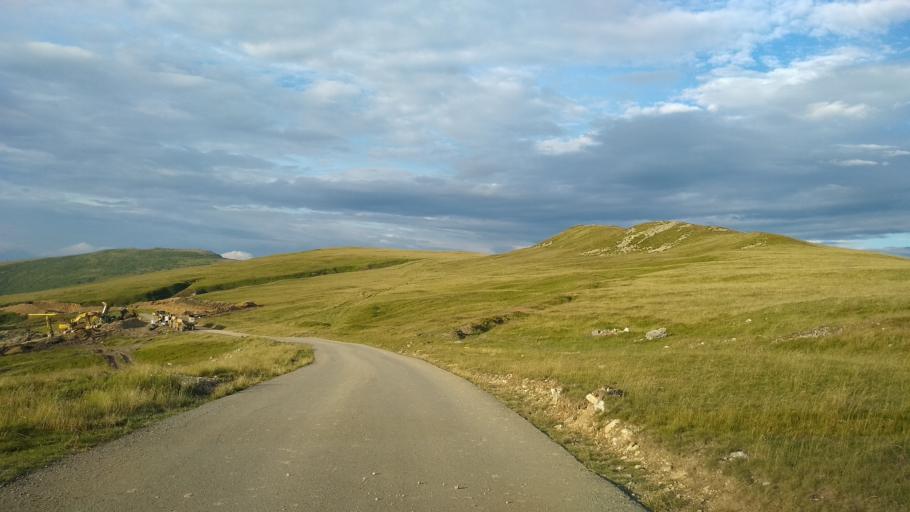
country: RO
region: Hunedoara
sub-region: Municipiul  Vulcan
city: Jiu-Paroseni
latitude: 45.2999
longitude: 23.3101
